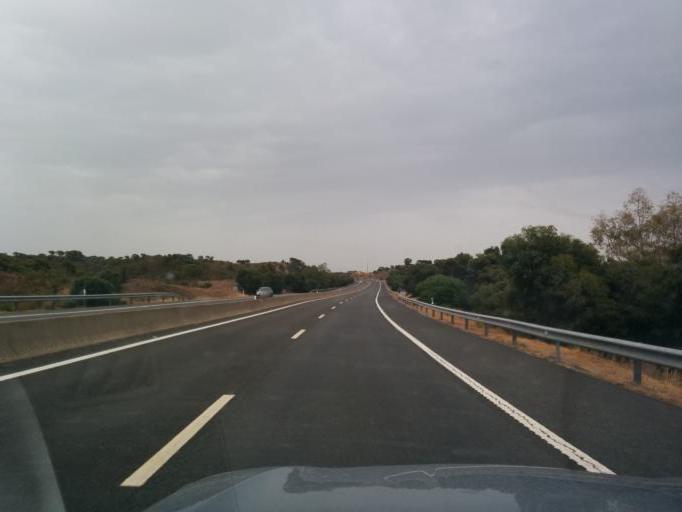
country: PT
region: Faro
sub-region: Tavira
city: Tavira
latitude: 37.1795
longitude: -7.5911
